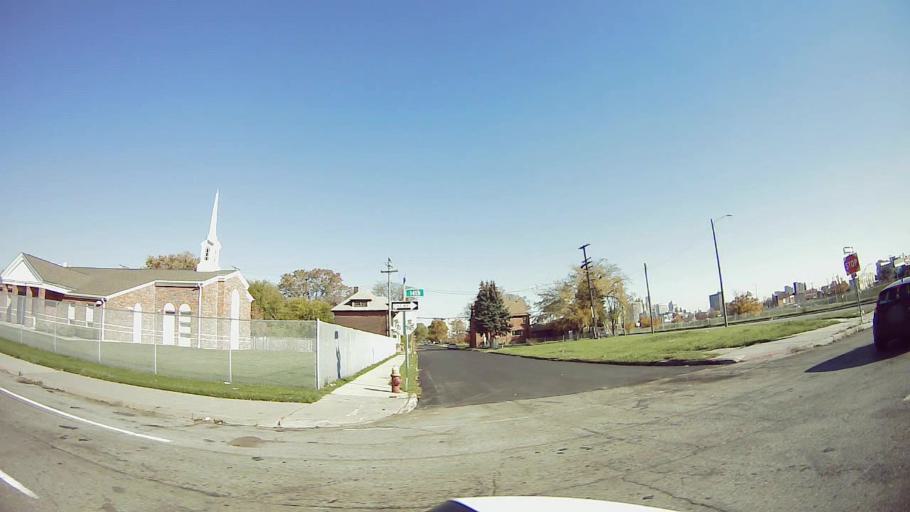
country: US
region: Michigan
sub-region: Wayne County
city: Detroit
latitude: 42.3317
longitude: -83.0765
